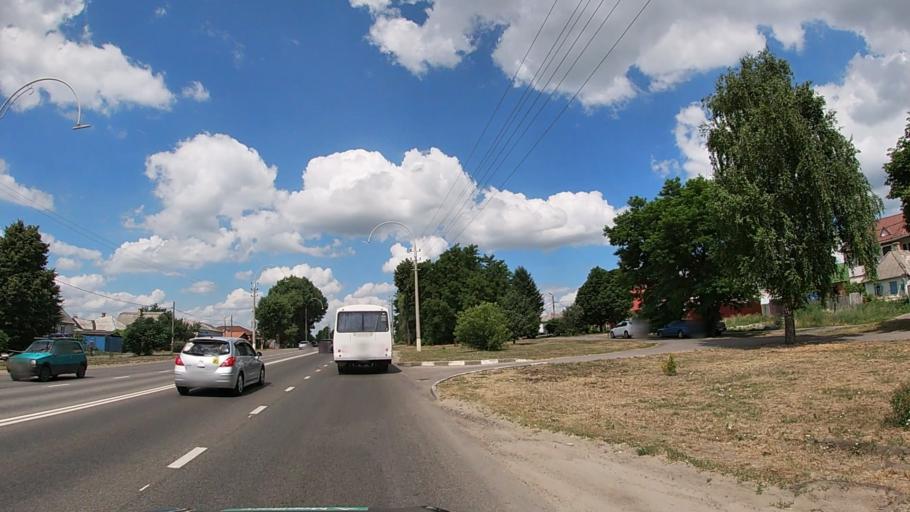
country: RU
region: Belgorod
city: Severnyy
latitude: 50.6258
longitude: 36.4975
